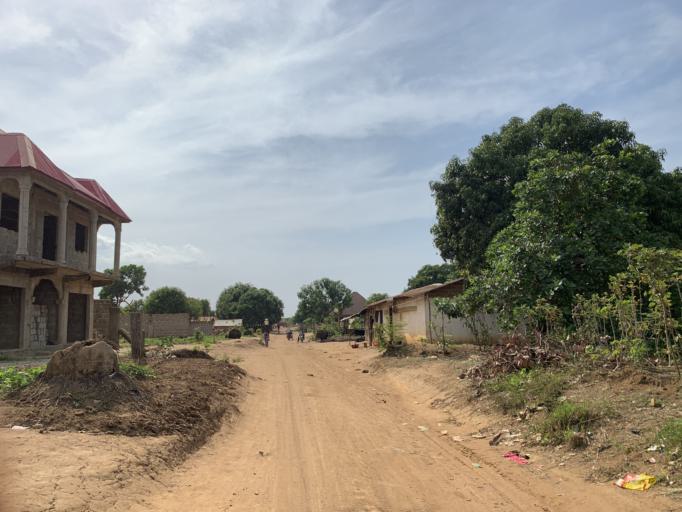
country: SL
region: Western Area
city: Waterloo
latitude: 8.3448
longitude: -13.0497
